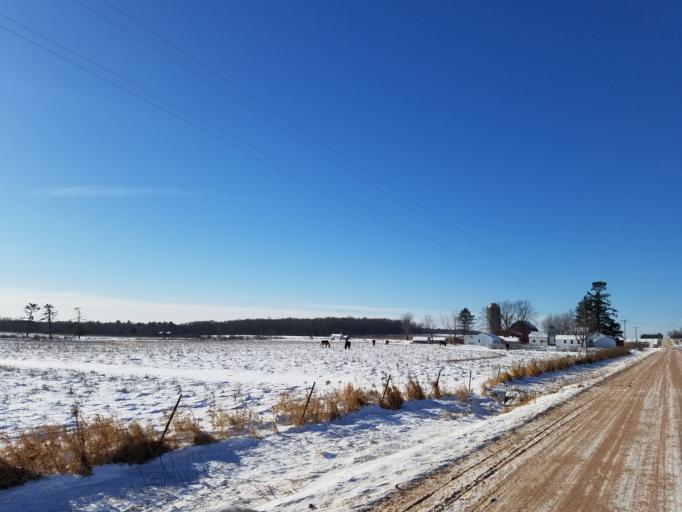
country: US
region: Wisconsin
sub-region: Clark County
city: Neillsville
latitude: 44.5681
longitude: -90.4105
